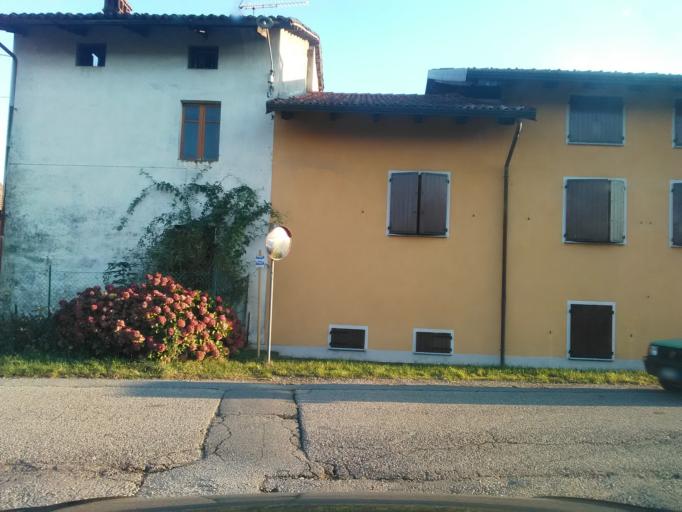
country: IT
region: Piedmont
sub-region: Provincia di Biella
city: Salussola
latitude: 45.4395
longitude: 8.1005
